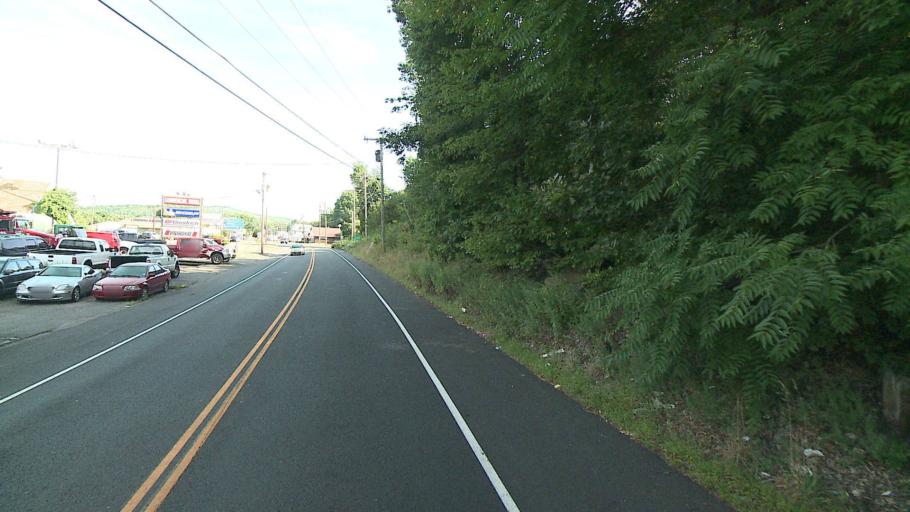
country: US
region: Connecticut
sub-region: New Haven County
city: Waterbury
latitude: 41.5805
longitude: -73.0489
